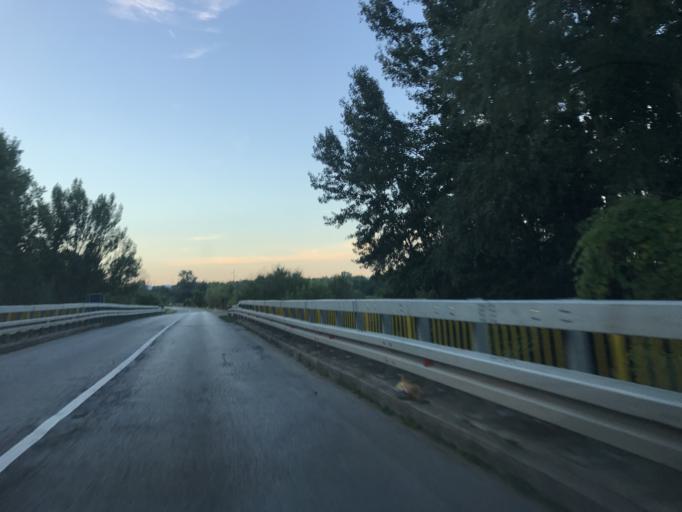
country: RS
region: Central Serbia
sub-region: Branicevski Okrug
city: Veliko Gradiste
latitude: 44.7030
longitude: 21.5306
